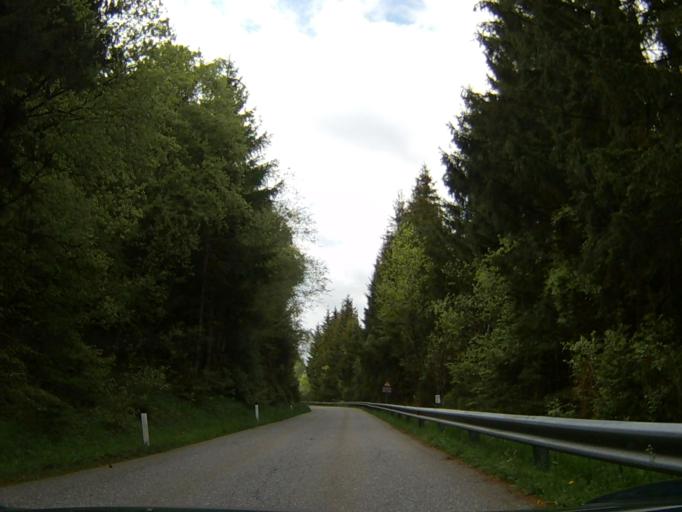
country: AT
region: Carinthia
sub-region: Politischer Bezirk Villach Land
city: Stockenboi
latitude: 46.7388
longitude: 13.5673
